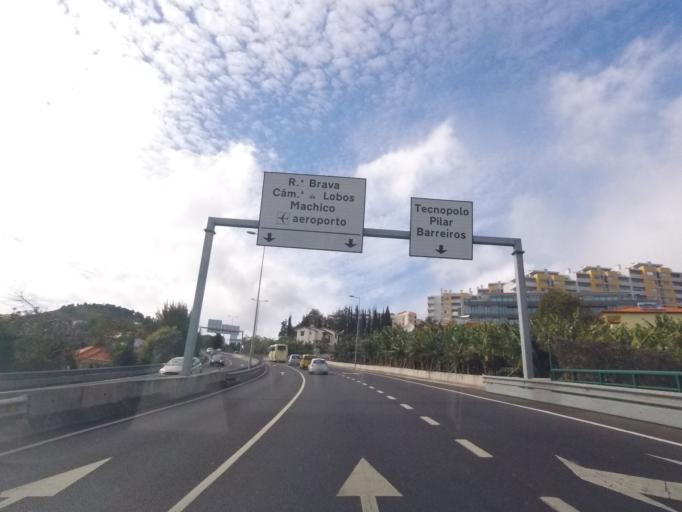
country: PT
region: Madeira
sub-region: Funchal
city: Nossa Senhora do Monte
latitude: 32.6539
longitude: -16.9293
